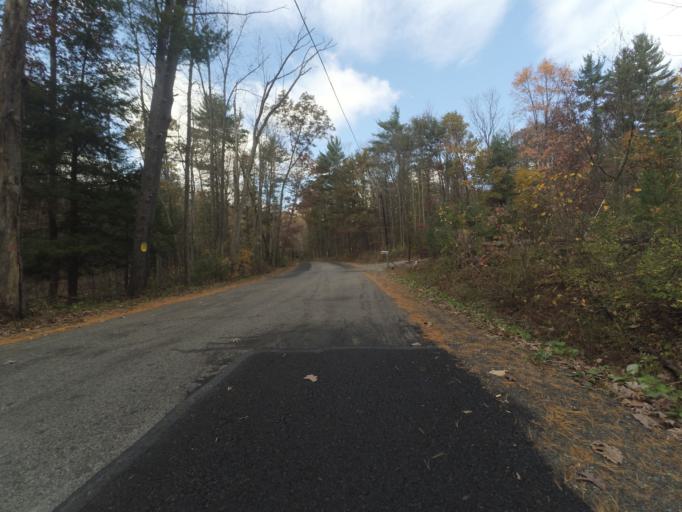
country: US
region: Pennsylvania
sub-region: Centre County
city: Stormstown
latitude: 40.8586
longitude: -77.9834
